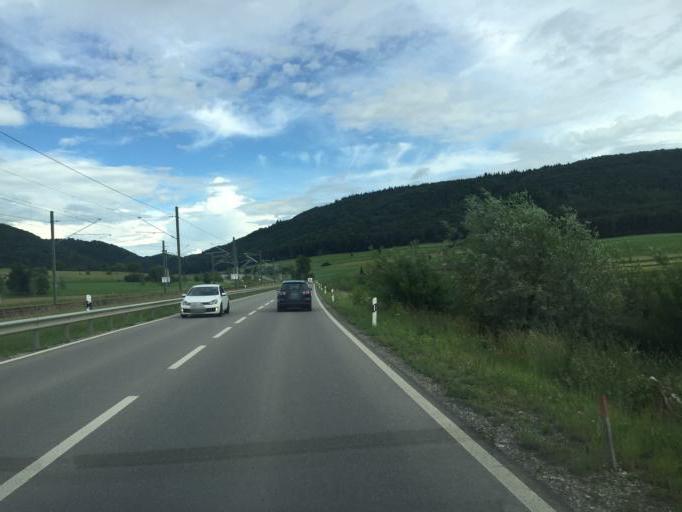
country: CH
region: Schaffhausen
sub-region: Bezirk Oberklettgau
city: Neunkirch
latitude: 47.6873
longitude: 8.5049
